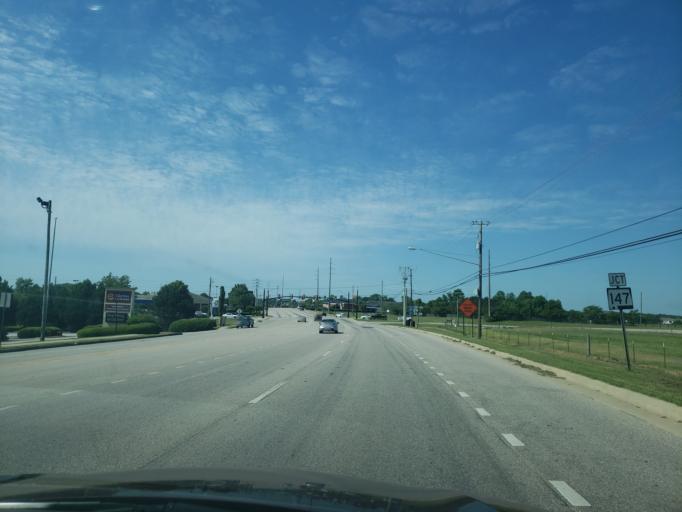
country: US
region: Alabama
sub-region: Lee County
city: Auburn
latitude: 32.5790
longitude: -85.4971
